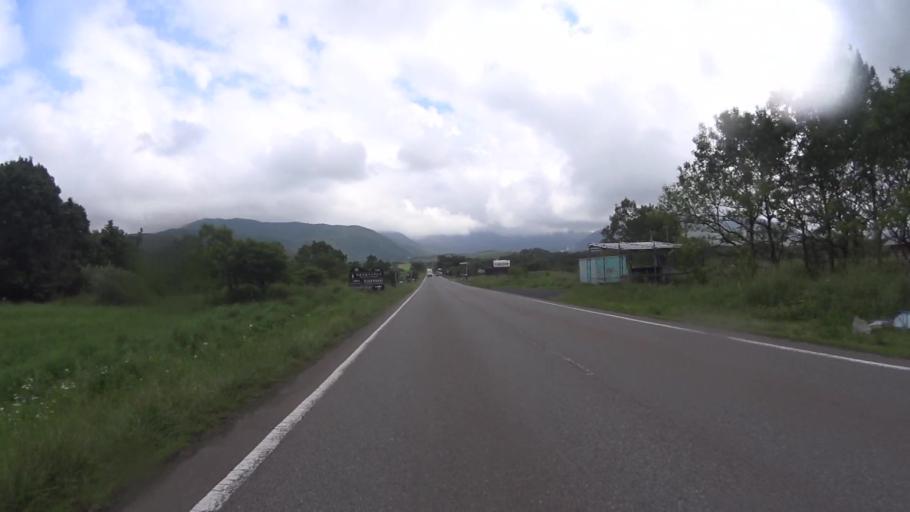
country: JP
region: Oita
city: Tsukawaki
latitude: 33.1548
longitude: 131.2409
